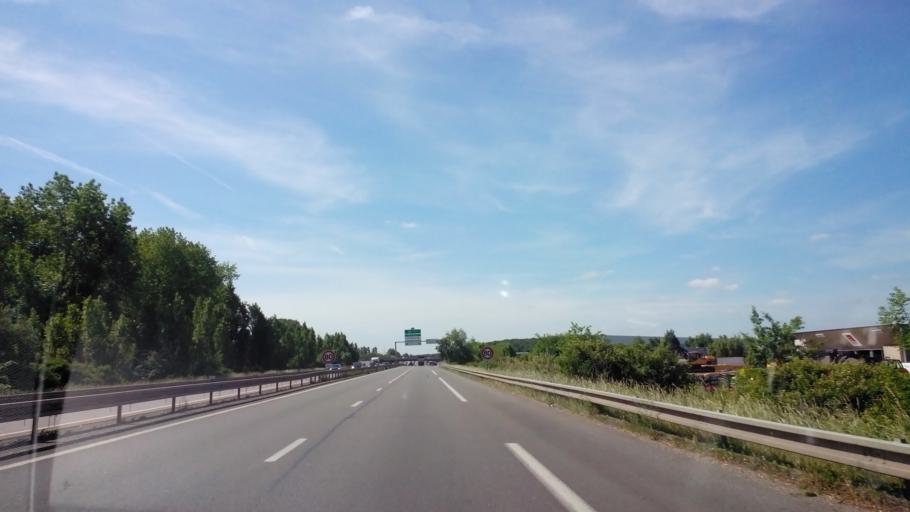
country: FR
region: Lorraine
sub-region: Departement de la Moselle
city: Saint-Julien-les-Metz
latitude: 49.1134
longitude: 6.2350
